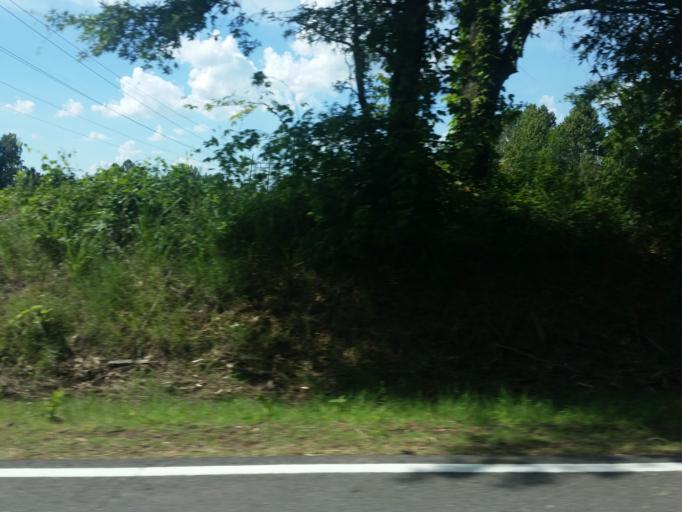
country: US
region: Tennessee
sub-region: Gibson County
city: Milan
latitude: 35.9771
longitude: -88.8041
